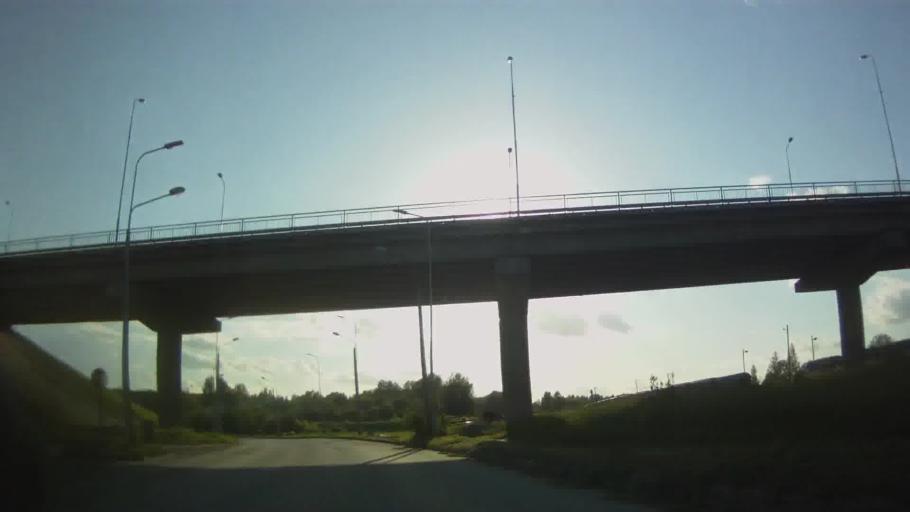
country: LV
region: Rezekne
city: Rezekne
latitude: 56.5199
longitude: 27.3399
